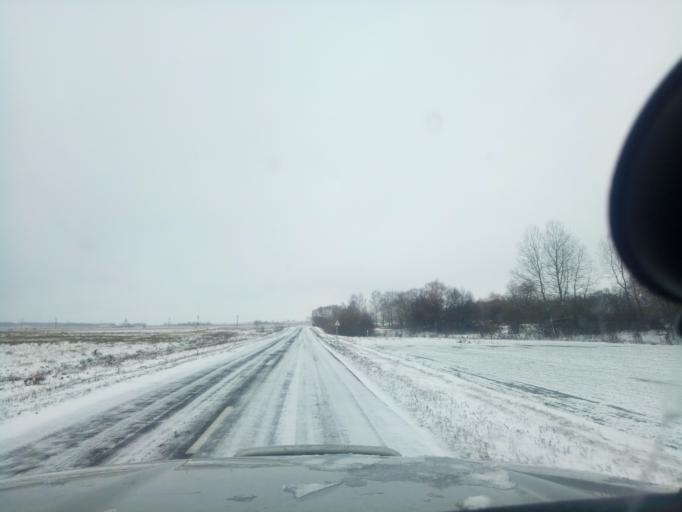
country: BY
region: Minsk
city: Klyetsk
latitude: 53.0550
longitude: 26.7852
